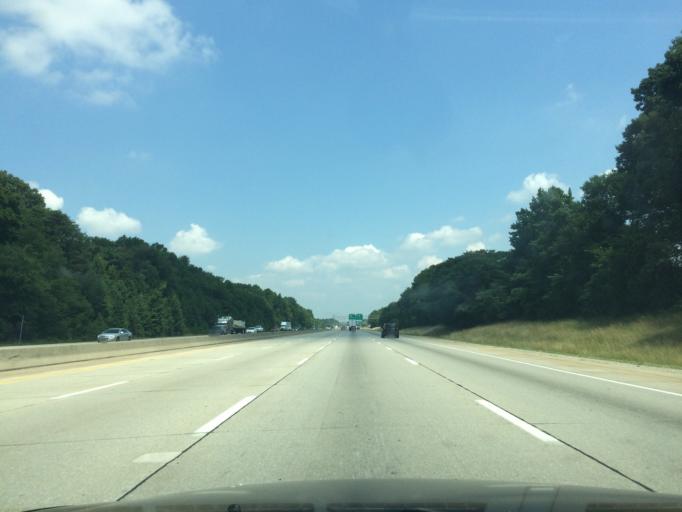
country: US
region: Kentucky
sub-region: Jefferson County
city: Heritage Creek
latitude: 38.1021
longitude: -85.7009
